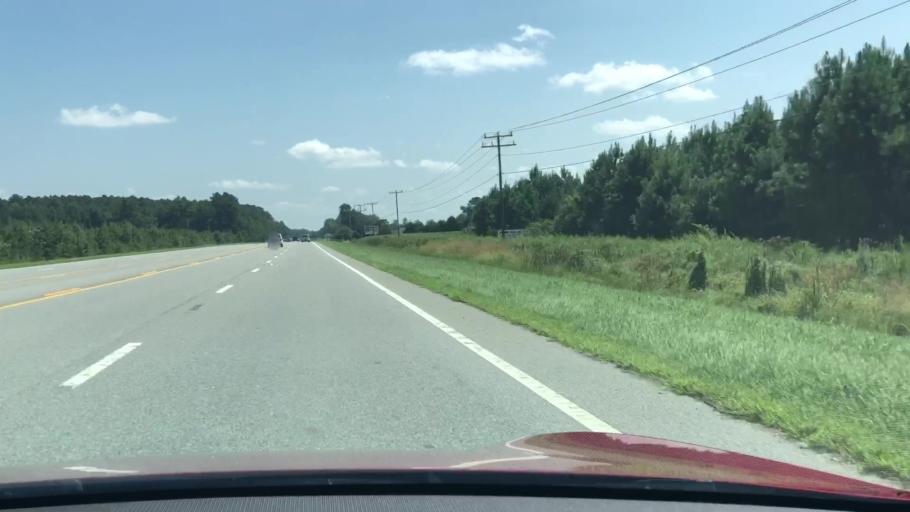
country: US
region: North Carolina
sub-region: Currituck County
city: Moyock
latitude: 36.4770
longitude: -76.1264
